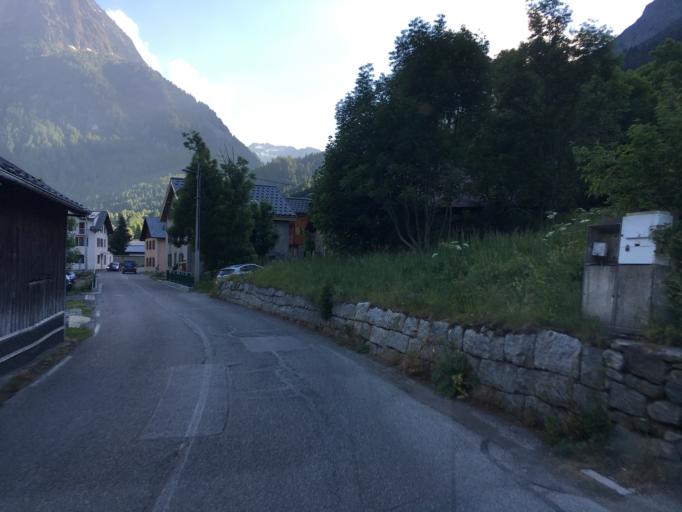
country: FR
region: Rhone-Alpes
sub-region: Departement de la Haute-Savoie
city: Chamonix-Mont-Blanc
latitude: 46.0272
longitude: 6.9254
